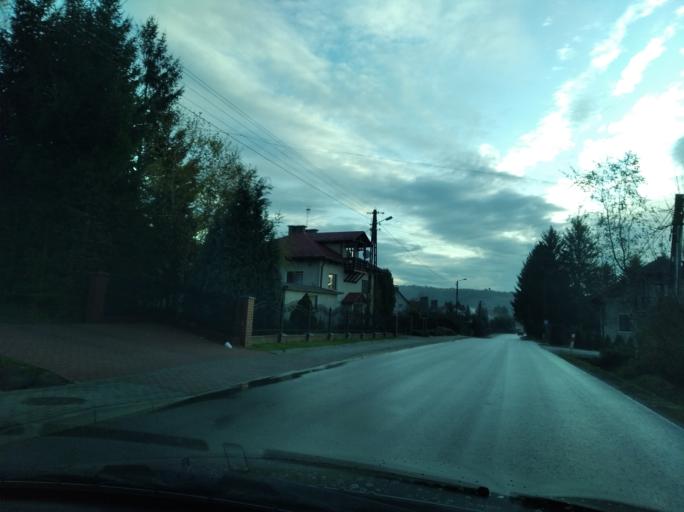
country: PL
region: Subcarpathian Voivodeship
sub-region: Powiat rzeszowski
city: Lubenia
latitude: 49.9430
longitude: 21.9242
